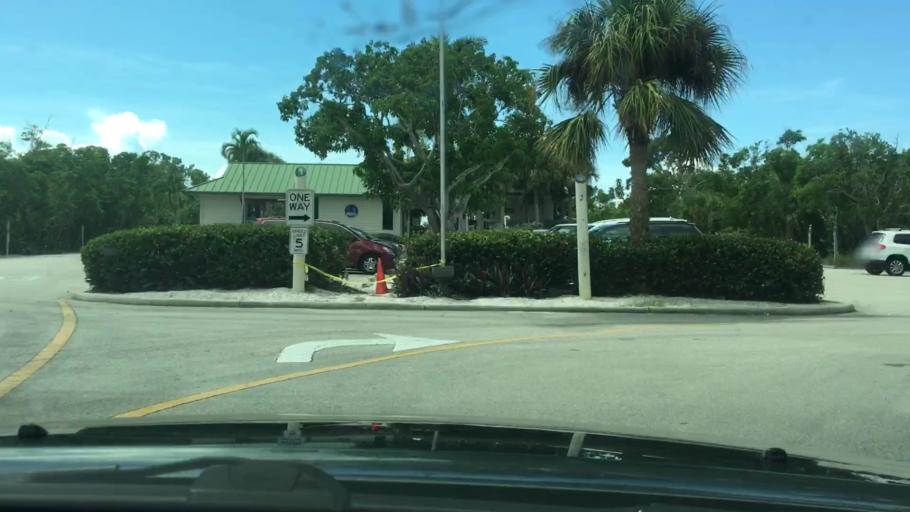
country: US
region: Florida
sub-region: Collier County
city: Marco
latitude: 25.9494
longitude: -81.7427
